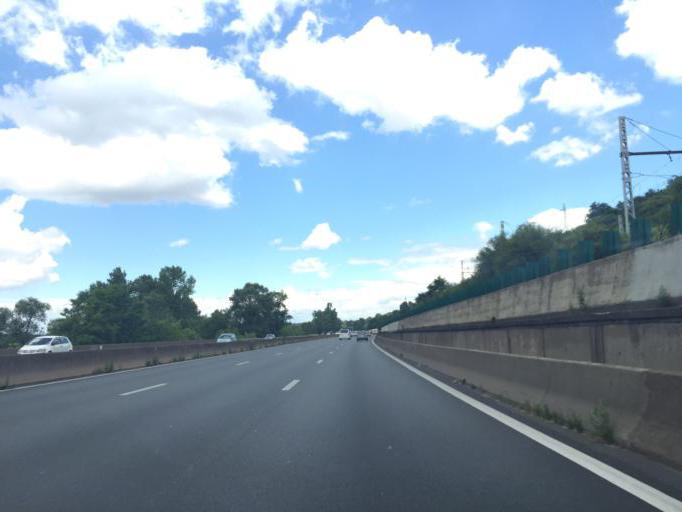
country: FR
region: Rhone-Alpes
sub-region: Departement du Rhone
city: Grigny
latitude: 45.6049
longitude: 4.7993
